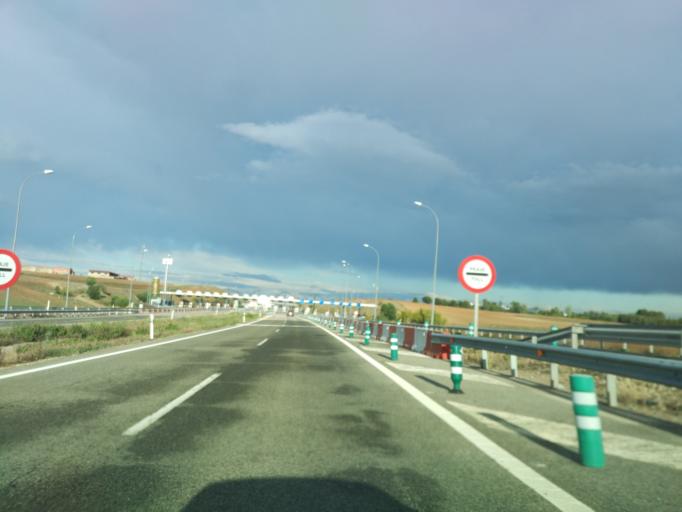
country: ES
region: Madrid
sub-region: Provincia de Madrid
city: Ajalvir
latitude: 40.5083
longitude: -3.4895
